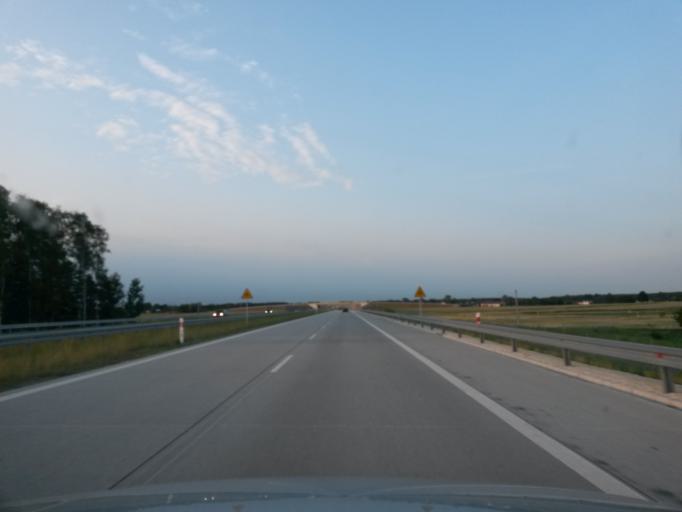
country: PL
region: Lodz Voivodeship
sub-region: Powiat wieruszowski
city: Lututow
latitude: 51.3471
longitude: 18.5085
